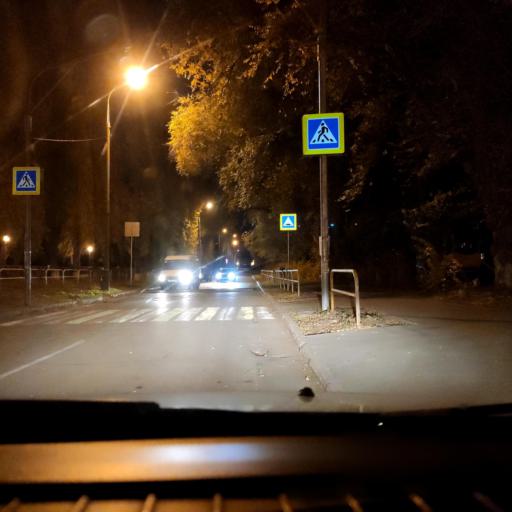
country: RU
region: Samara
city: Tol'yatti
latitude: 53.5253
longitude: 49.2672
